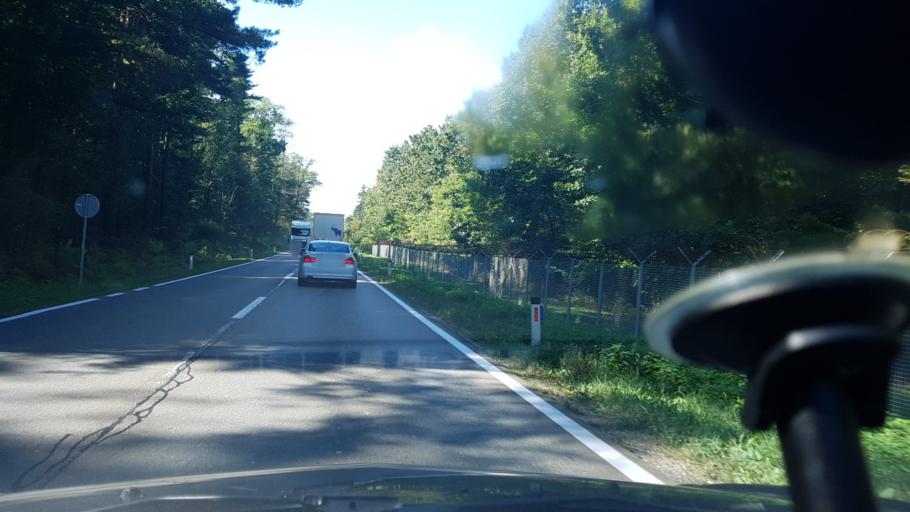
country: SI
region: Kidricevo
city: Kidricevo
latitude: 46.4121
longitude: 15.8062
